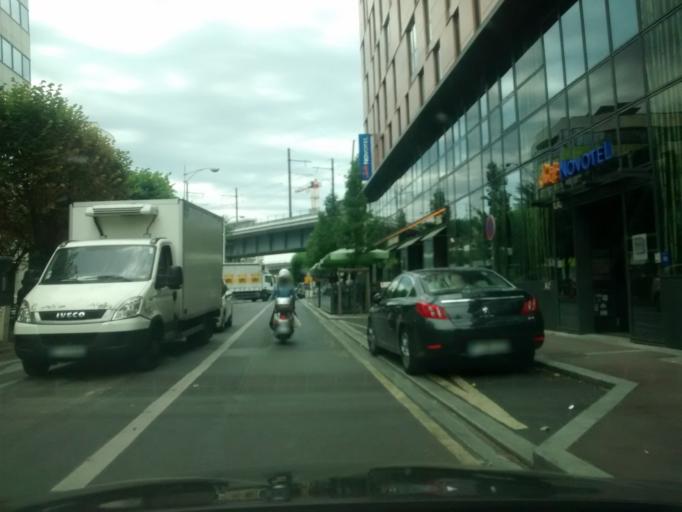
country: FR
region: Ile-de-France
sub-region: Departement des Hauts-de-Seine
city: Boulogne-Billancourt
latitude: 48.8290
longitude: 2.2635
